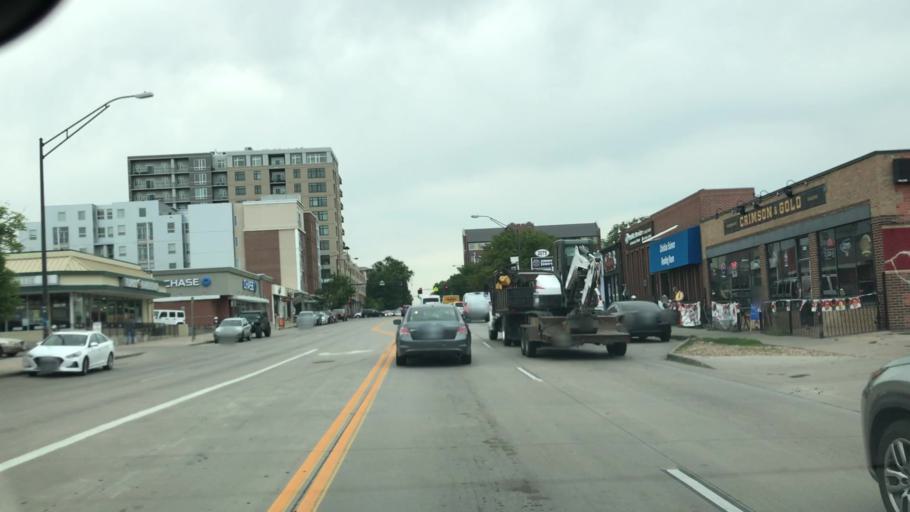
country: US
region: Colorado
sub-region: Arapahoe County
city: Glendale
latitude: 39.6800
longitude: -104.9594
